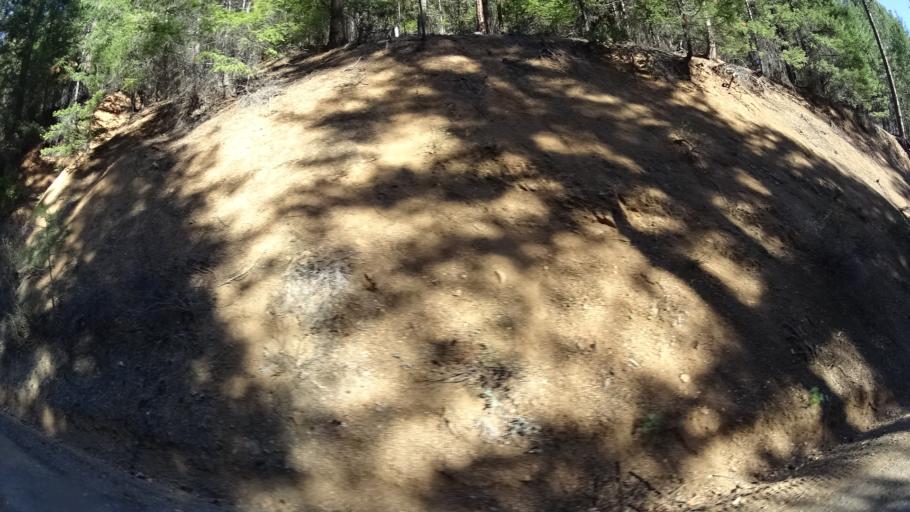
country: US
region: California
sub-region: Siskiyou County
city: Yreka
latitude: 41.7312
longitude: -122.7268
